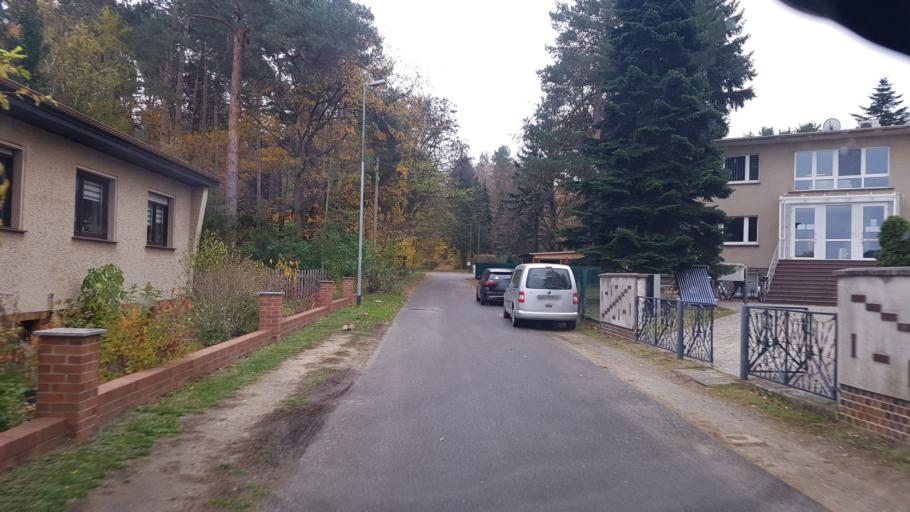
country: DE
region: Brandenburg
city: Crinitz
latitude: 51.7372
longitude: 13.7672
